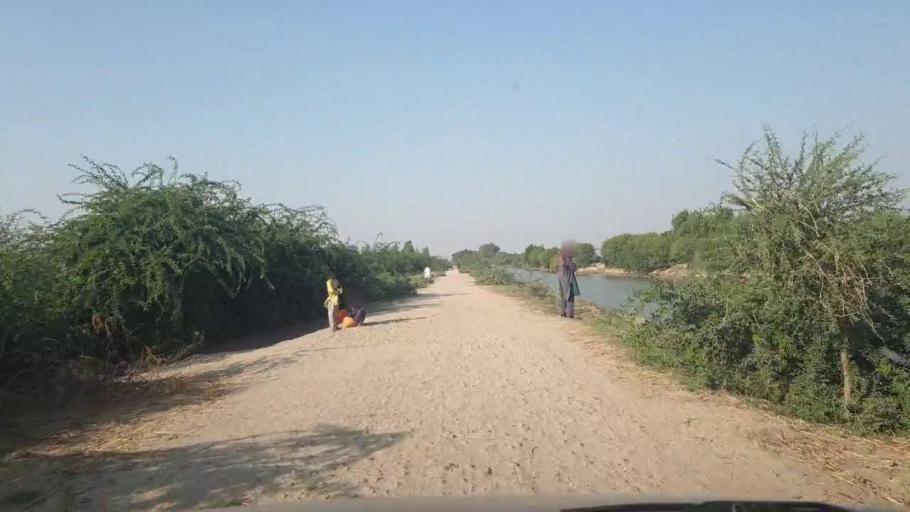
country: PK
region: Sindh
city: Badin
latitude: 24.6486
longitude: 68.8152
